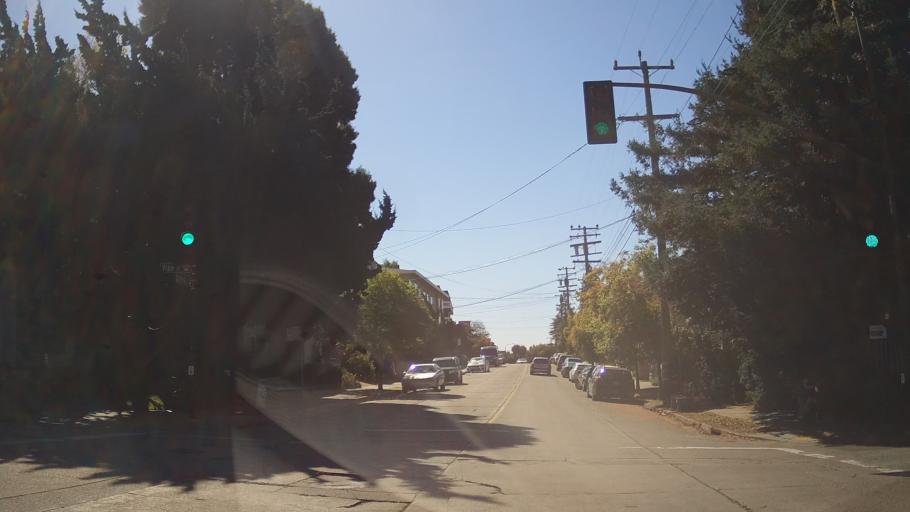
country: US
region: California
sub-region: Alameda County
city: Berkeley
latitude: 37.8806
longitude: -122.2671
